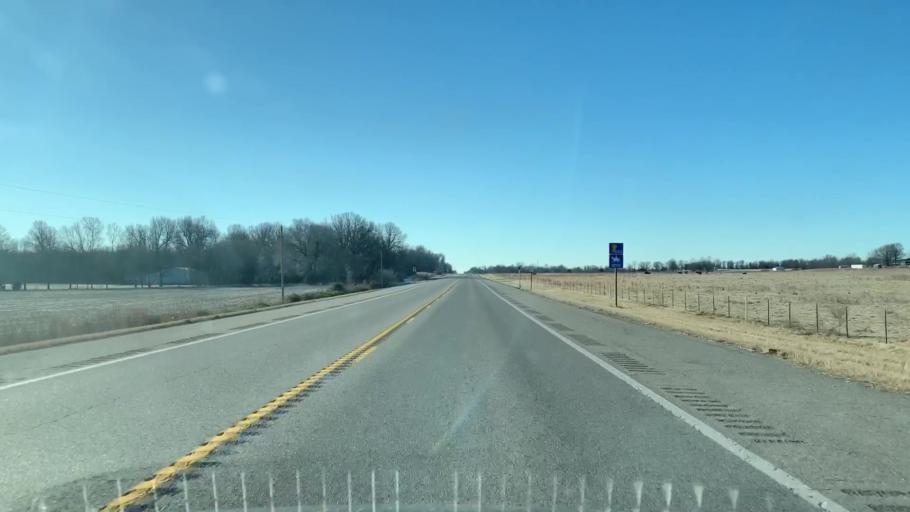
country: US
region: Kansas
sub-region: Crawford County
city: Pittsburg
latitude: 37.3076
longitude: -94.7055
